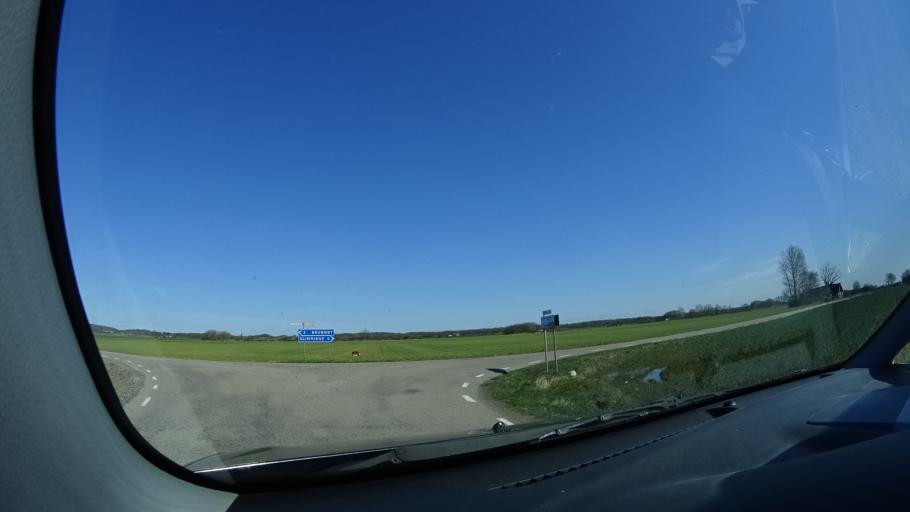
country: SE
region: Skane
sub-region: Hoganas Kommun
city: Hoganas
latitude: 56.2382
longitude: 12.5863
